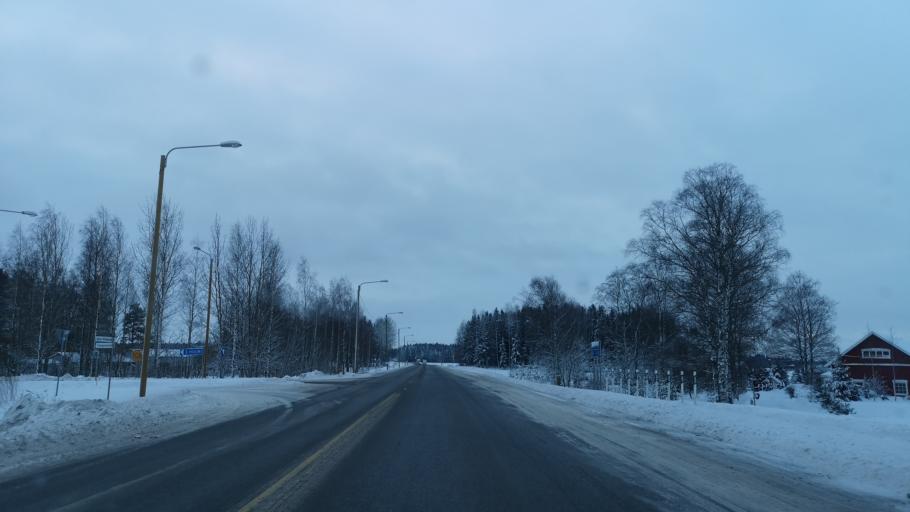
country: FI
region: Varsinais-Suomi
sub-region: Loimaa
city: Loimaa
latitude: 60.8851
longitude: 23.0894
